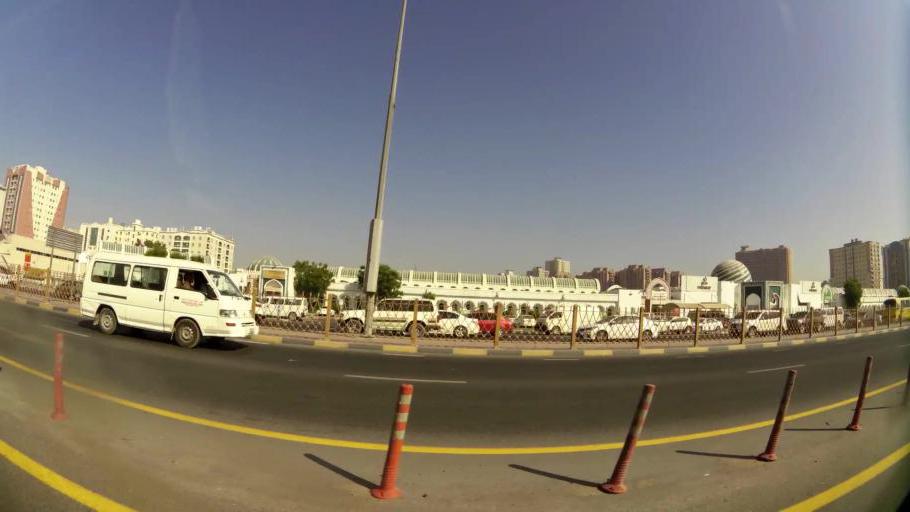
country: AE
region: Ajman
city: Ajman
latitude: 25.3814
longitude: 55.4628
